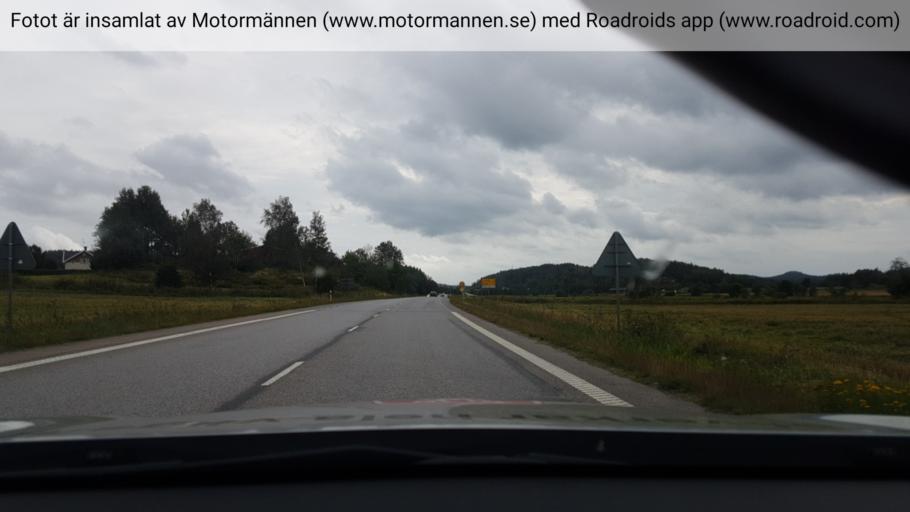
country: SE
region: Vaestra Goetaland
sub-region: Munkedals Kommun
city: Munkedal
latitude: 58.5073
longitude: 11.5756
